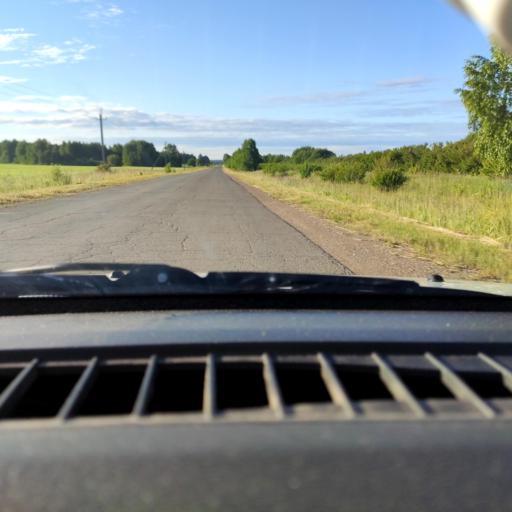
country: RU
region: Perm
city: Uinskoye
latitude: 57.0999
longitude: 56.5424
